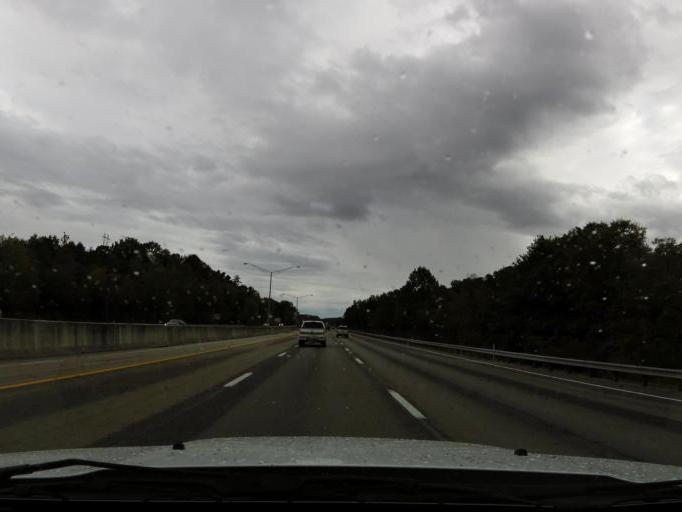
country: US
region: Kentucky
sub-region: Laurel County
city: London
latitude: 37.1511
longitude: -84.1119
